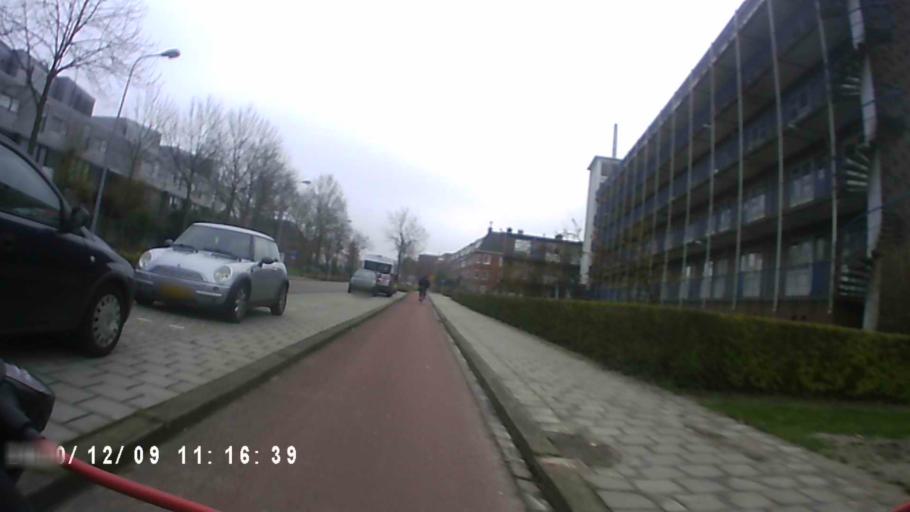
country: NL
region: Groningen
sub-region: Gemeente Groningen
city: Groningen
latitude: 53.2184
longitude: 6.5437
